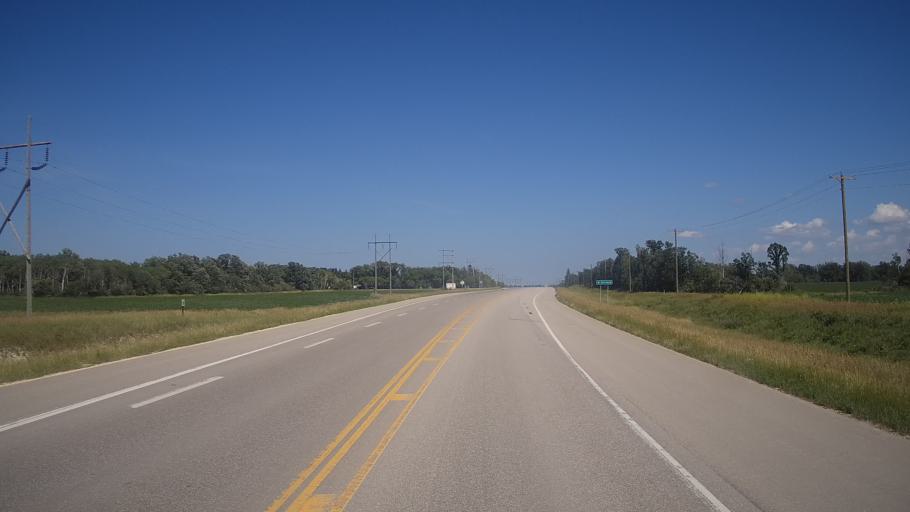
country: CA
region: Manitoba
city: Stonewall
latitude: 50.1228
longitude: -97.3389
